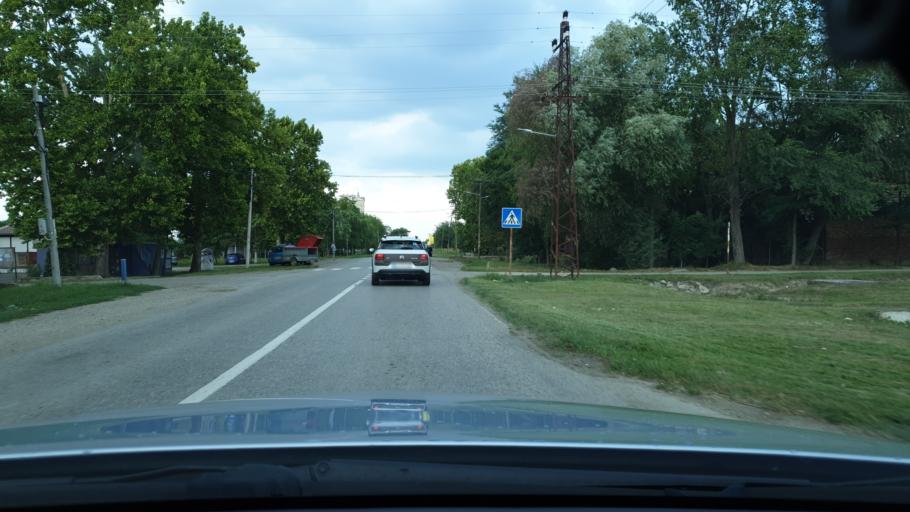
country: RS
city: Boka
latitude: 45.3535
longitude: 20.8333
